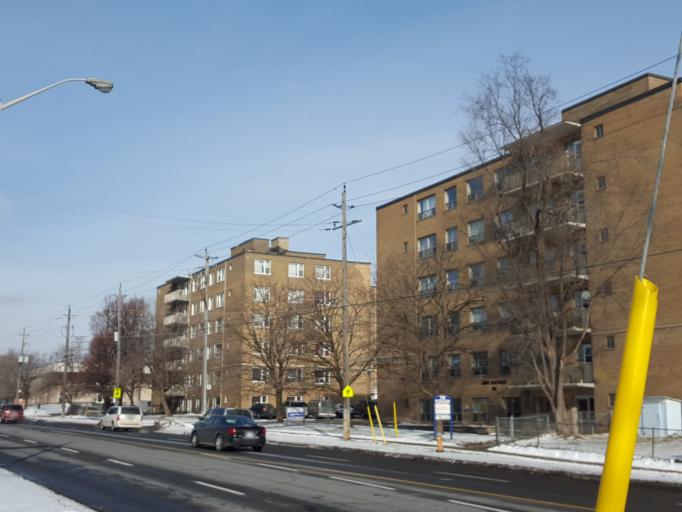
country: CA
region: Ontario
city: Scarborough
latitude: 43.7277
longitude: -79.2662
